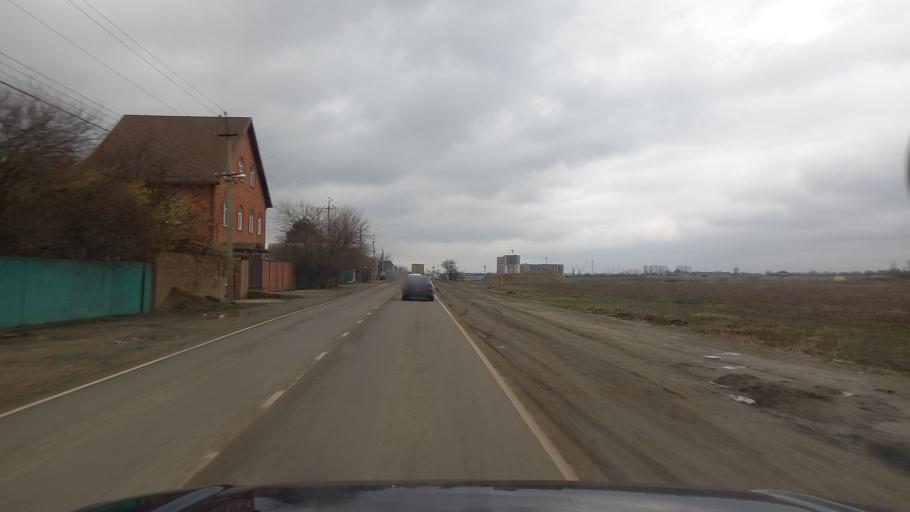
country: RU
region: Krasnodarskiy
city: Pashkovskiy
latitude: 45.0592
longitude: 39.1639
